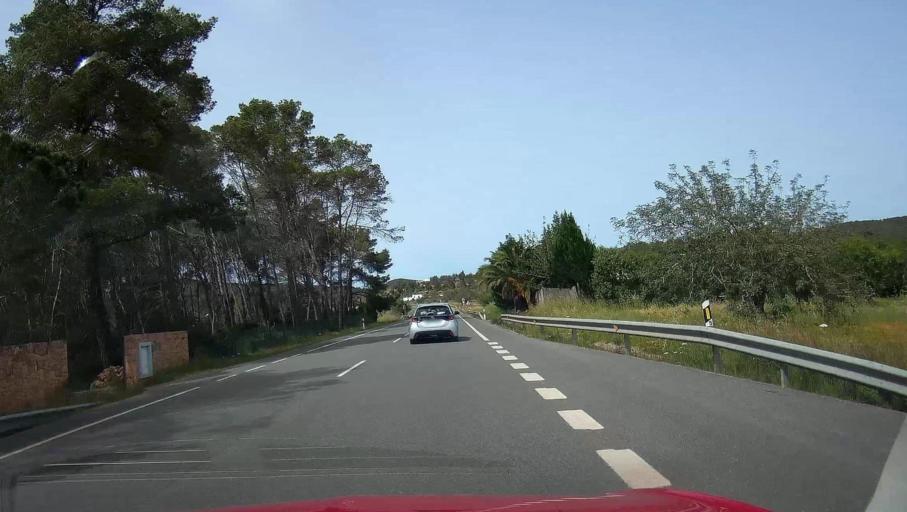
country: ES
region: Balearic Islands
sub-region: Illes Balears
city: Sant Joan de Labritja
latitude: 39.0599
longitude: 1.4942
